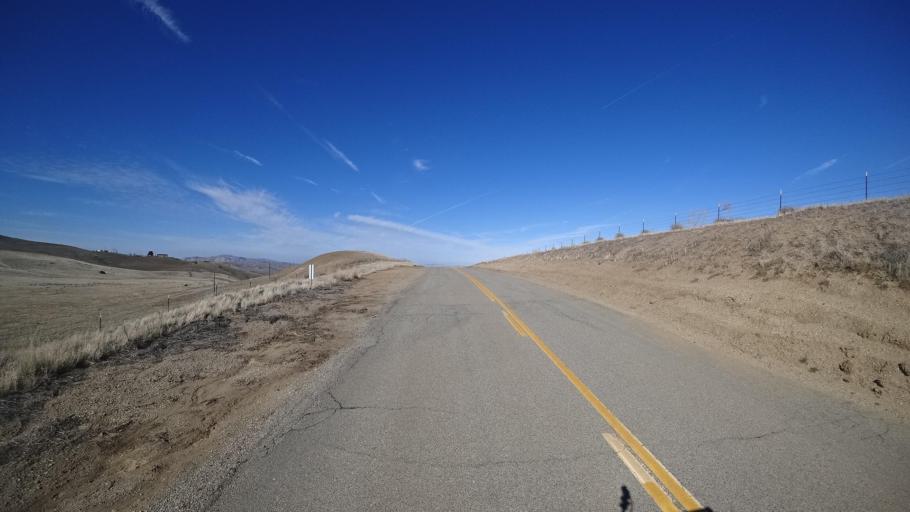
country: US
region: California
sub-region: Kern County
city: Maricopa
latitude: 34.9374
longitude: -119.4024
